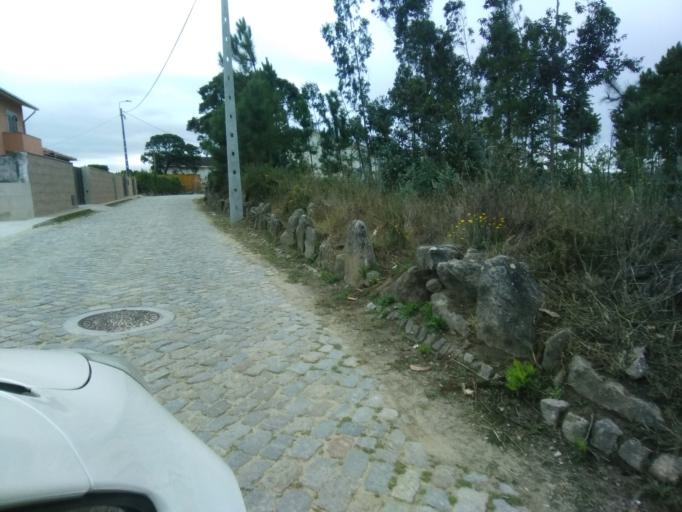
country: PT
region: Porto
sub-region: Matosinhos
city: Santa Cruz do Bispo
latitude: 41.2317
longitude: -8.7100
